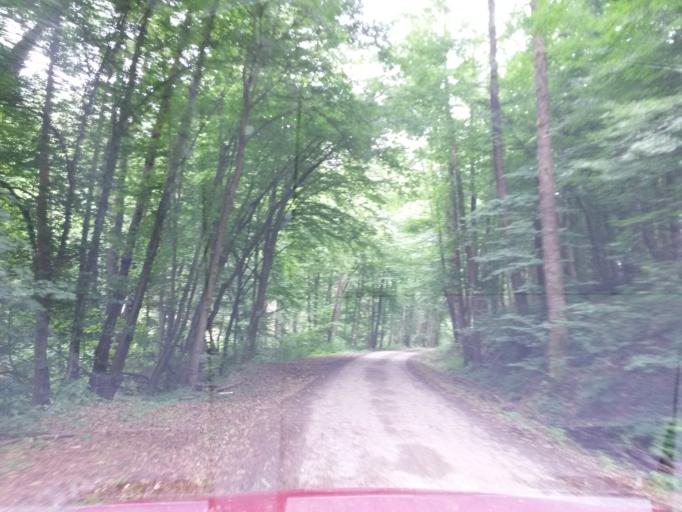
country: SK
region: Banskobystricky
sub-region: Okres Banska Bystrica
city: Zvolen
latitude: 48.5363
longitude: 19.2389
